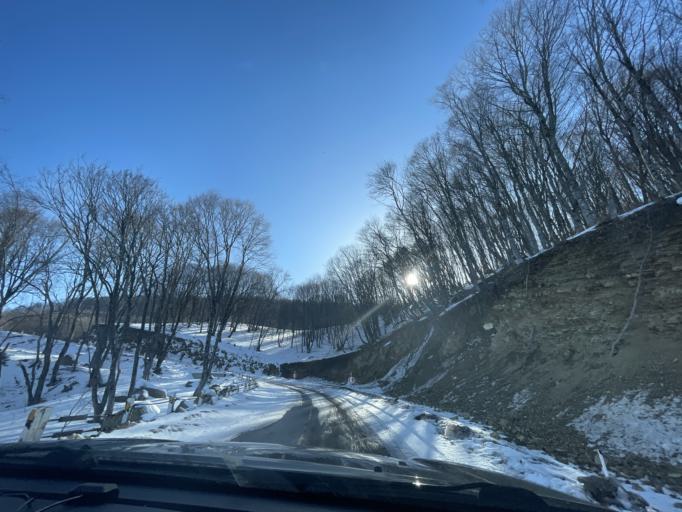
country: GE
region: Kvemo Kartli
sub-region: Tetri Tsqaro
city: Manglisi
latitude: 41.7725
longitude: 44.5065
